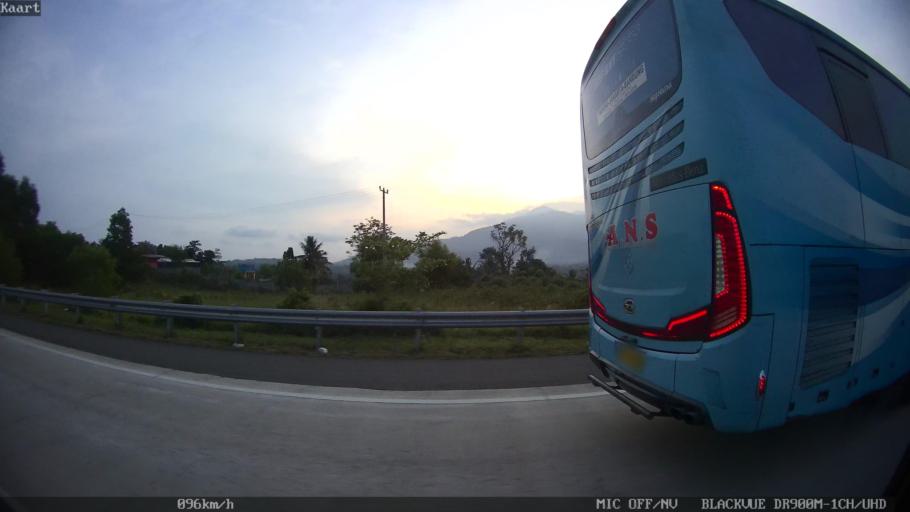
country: ID
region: Lampung
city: Penengahan
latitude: -5.7852
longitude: 105.7232
